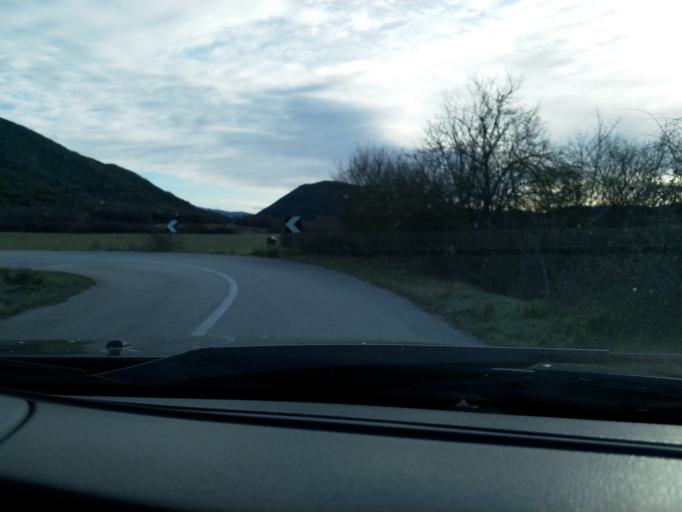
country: GR
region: Epirus
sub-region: Nomos Ioanninon
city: Asprangeloi
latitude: 39.8683
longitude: 20.7089
